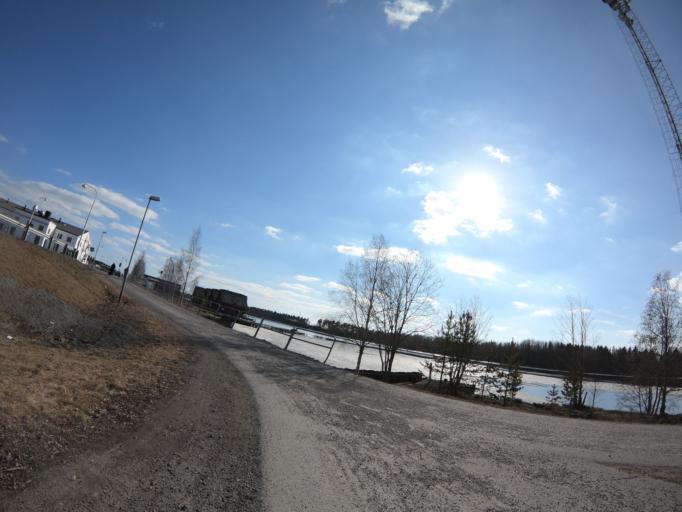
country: SE
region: Vaesterbotten
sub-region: Umea Kommun
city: Umea
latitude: 63.8010
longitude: 20.2996
